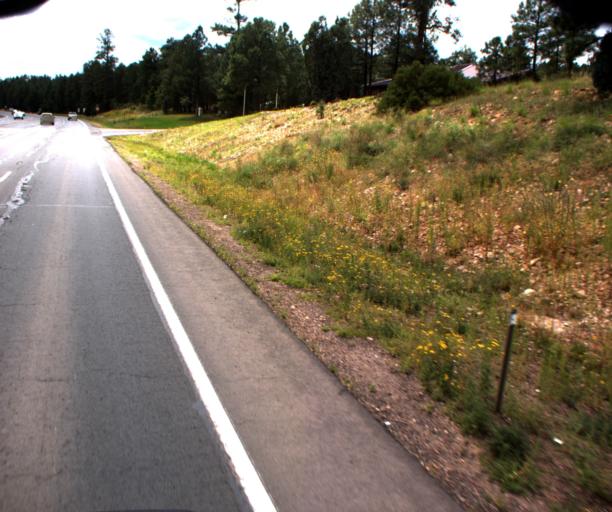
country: US
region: Arizona
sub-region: Navajo County
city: Show Low
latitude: 34.2264
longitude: -110.0287
